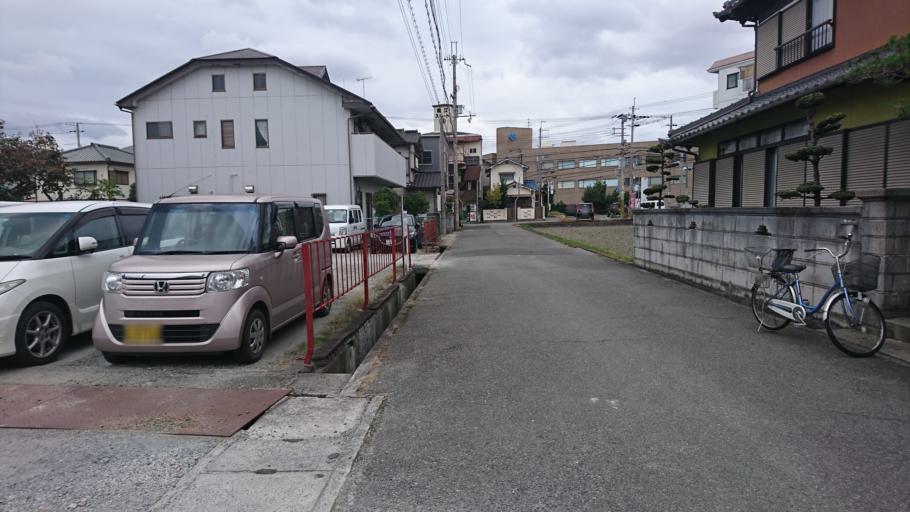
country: JP
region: Hyogo
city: Kakogawacho-honmachi
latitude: 34.7598
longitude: 134.8385
